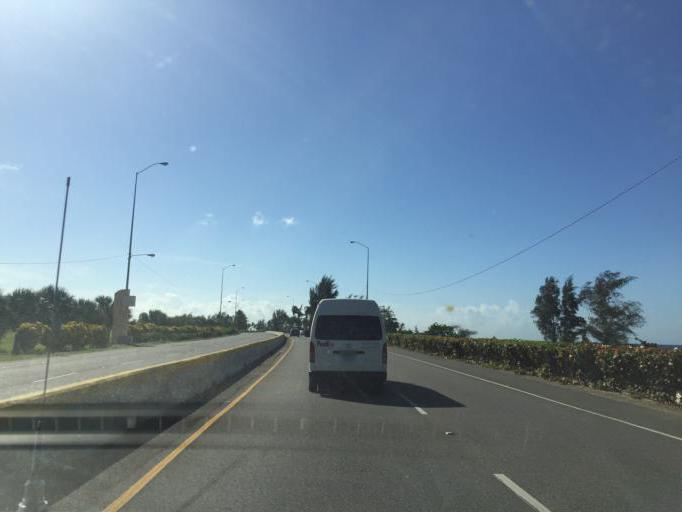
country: DO
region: Santo Domingo
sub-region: Santo Domingo
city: Boca Chica
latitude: 18.4411
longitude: -69.6816
